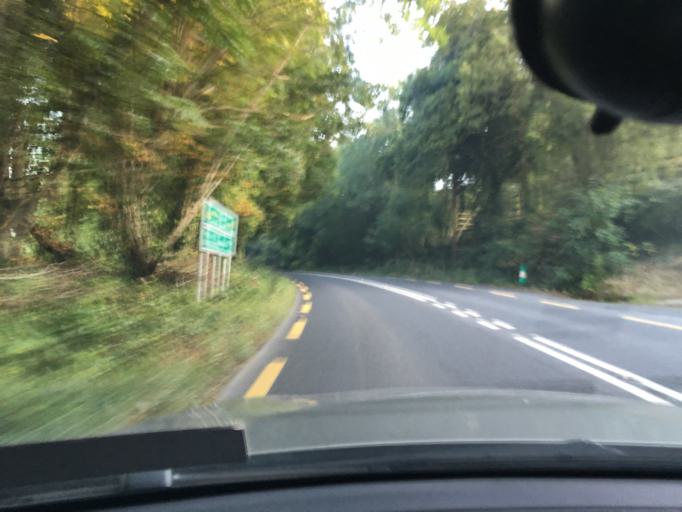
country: IE
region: Connaught
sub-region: County Galway
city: Moycullen
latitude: 53.3793
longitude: -9.2499
